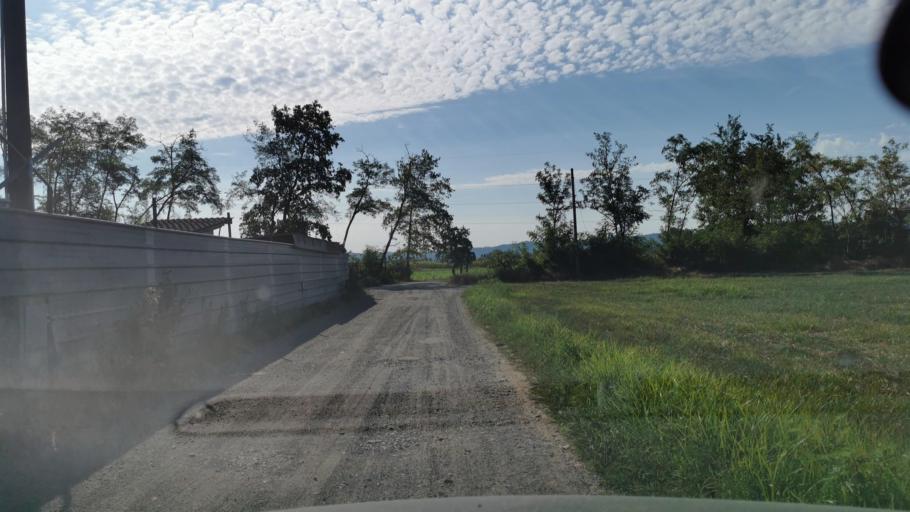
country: IT
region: Piedmont
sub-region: Provincia di Torino
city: Settimo Torinese
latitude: 45.1641
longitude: 7.7768
